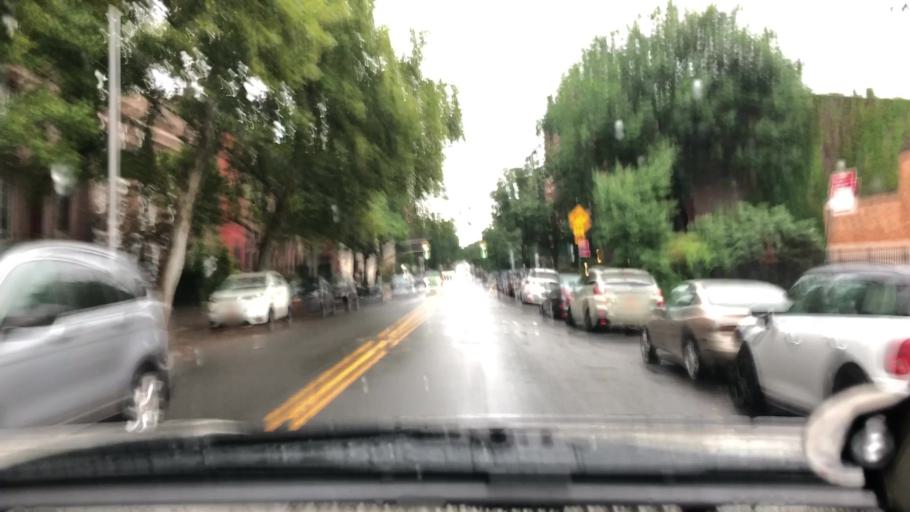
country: US
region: New York
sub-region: Kings County
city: Brooklyn
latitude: 40.6855
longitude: -73.9653
